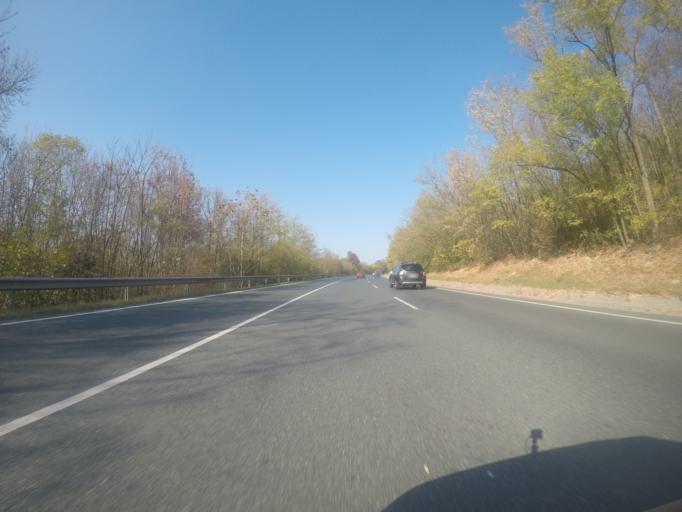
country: HU
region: Tolna
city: Madocsa
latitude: 46.6933
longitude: 18.8865
